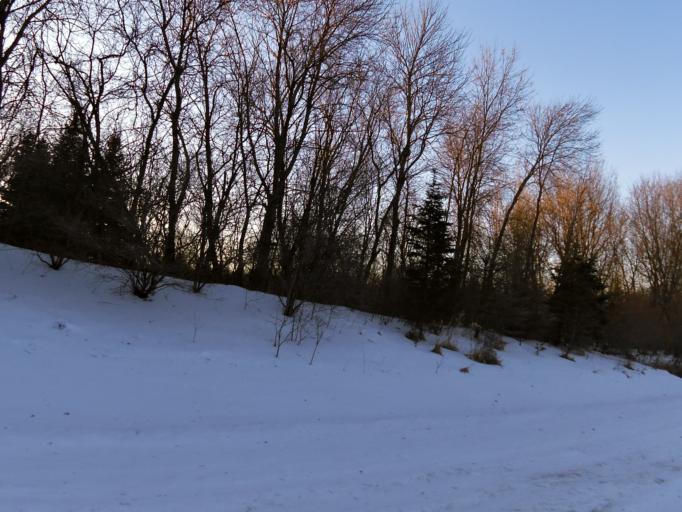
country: US
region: Minnesota
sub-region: Washington County
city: Lakeland
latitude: 44.9649
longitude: -92.8086
